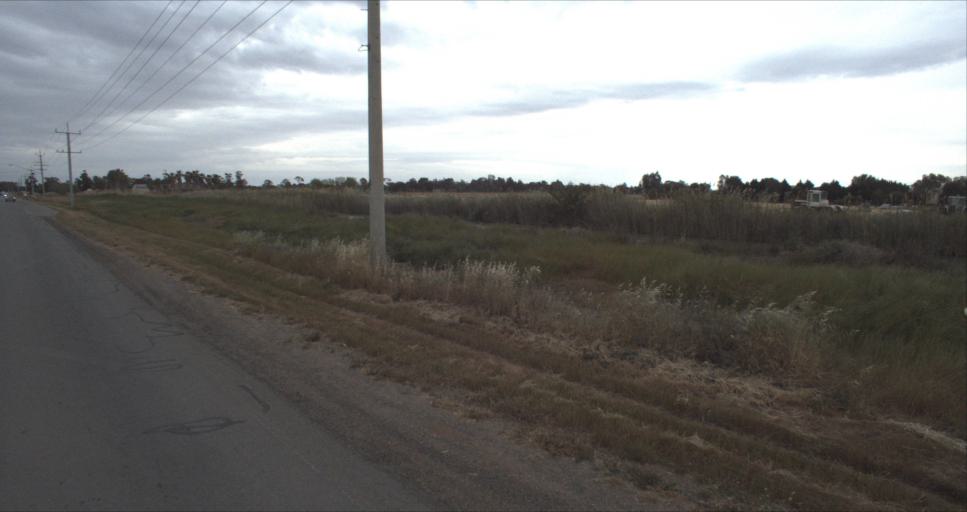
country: AU
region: New South Wales
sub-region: Leeton
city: Leeton
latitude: -34.5439
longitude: 146.3864
